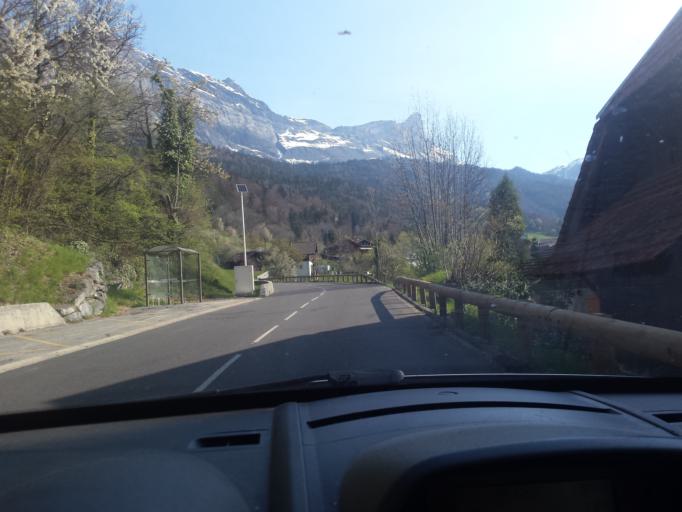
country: FR
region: Rhone-Alpes
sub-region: Departement de la Haute-Savoie
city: Passy
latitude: 45.9299
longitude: 6.7129
